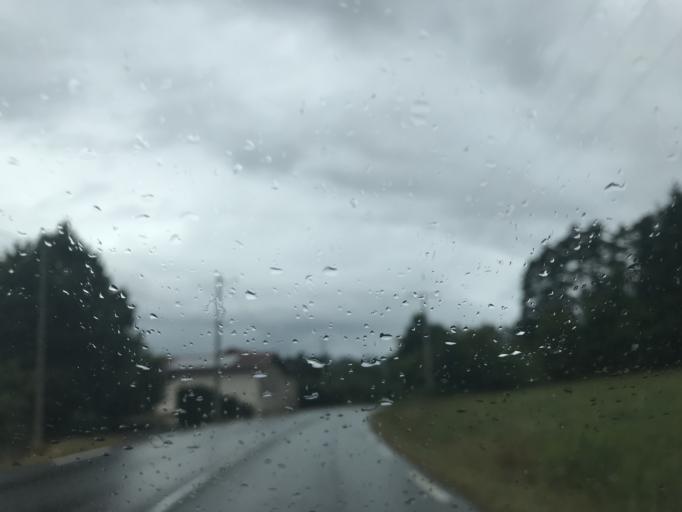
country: FR
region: Auvergne
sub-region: Departement du Puy-de-Dome
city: Ambert
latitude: 45.5798
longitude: 3.7363
